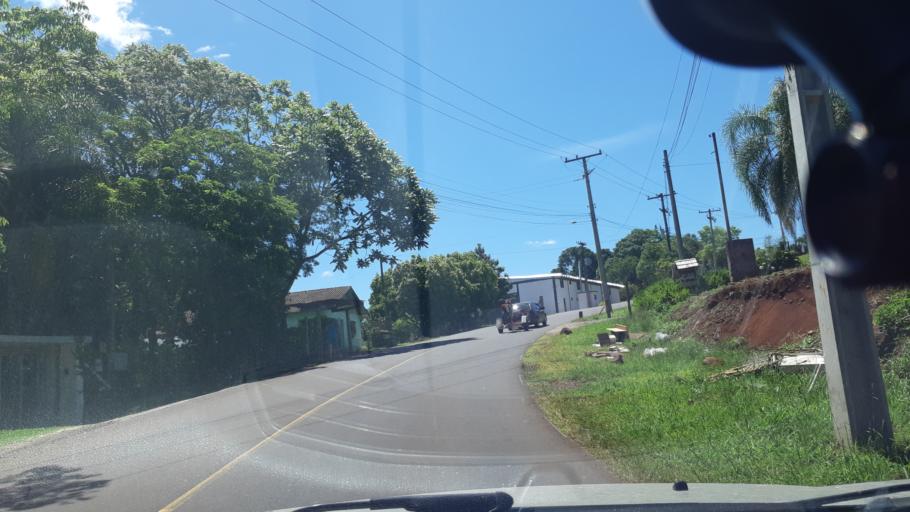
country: BR
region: Rio Grande do Sul
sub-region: Ivoti
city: Ivoti
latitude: -29.6211
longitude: -51.1120
